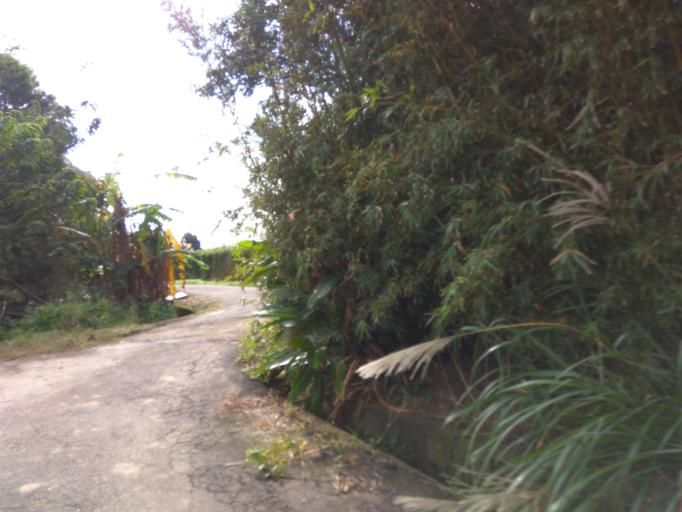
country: TW
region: Taiwan
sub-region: Hsinchu
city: Zhubei
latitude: 24.9554
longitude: 121.1079
